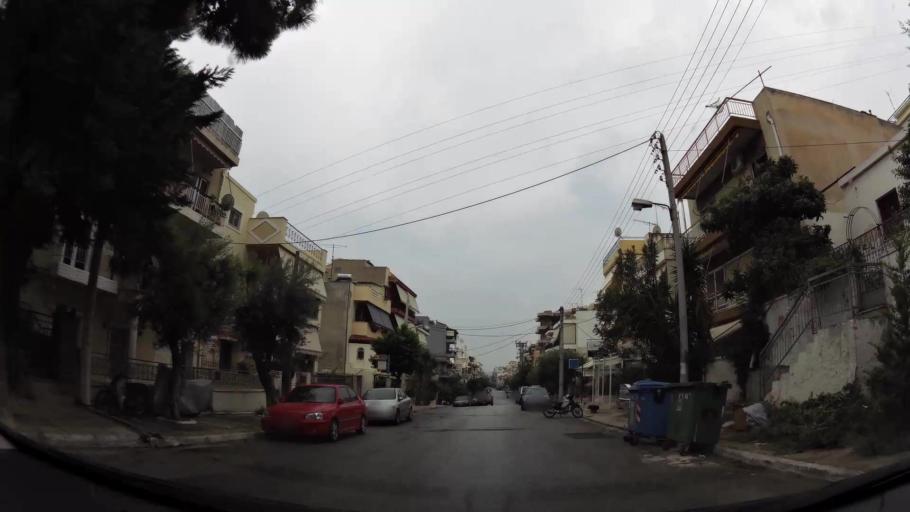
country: GR
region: Attica
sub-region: Nomos Piraios
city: Korydallos
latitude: 37.9923
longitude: 23.6507
